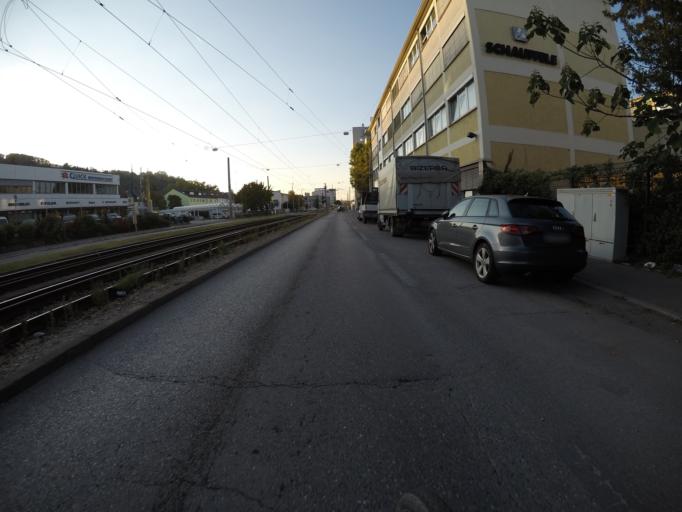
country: DE
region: Baden-Wuerttemberg
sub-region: Regierungsbezirk Stuttgart
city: Stuttgart-Ost
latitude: 48.7767
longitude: 9.2359
